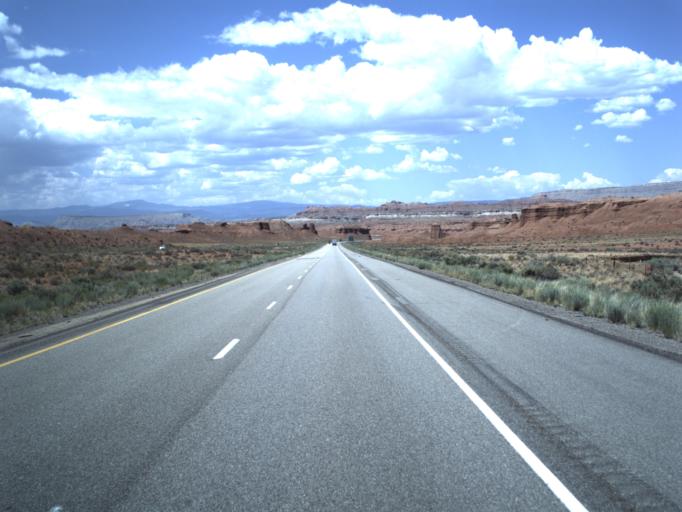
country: US
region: Utah
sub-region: Emery County
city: Ferron
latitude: 38.8474
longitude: -111.0341
